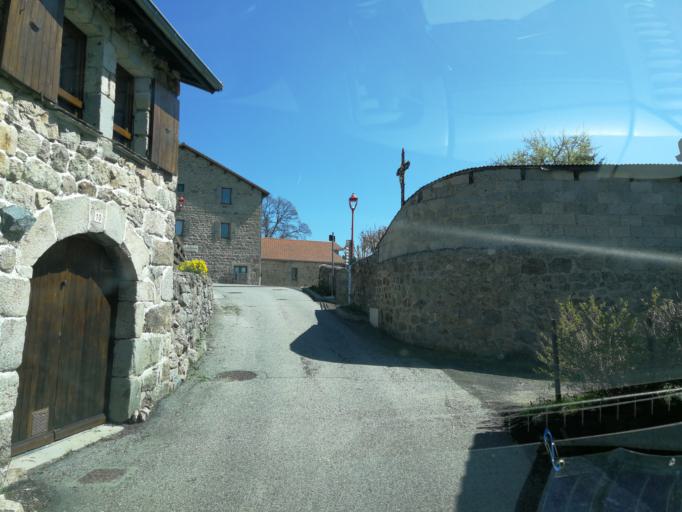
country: FR
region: Rhone-Alpes
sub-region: Departement de l'Ardeche
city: Le Cheylard
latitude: 44.9415
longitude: 4.4292
